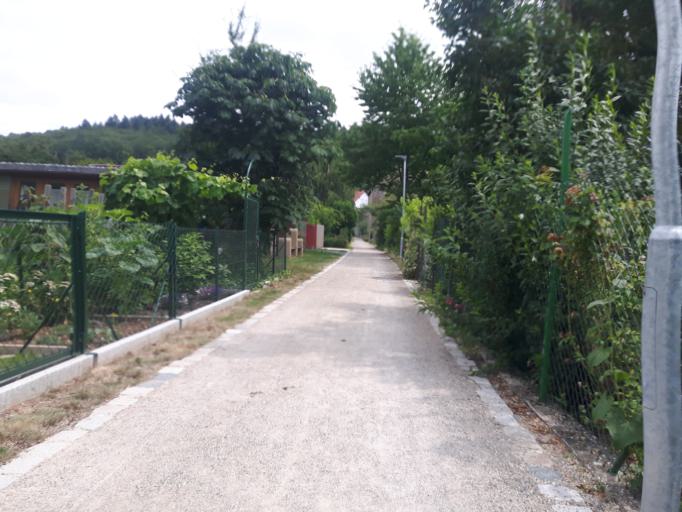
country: DE
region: Baden-Wuerttemberg
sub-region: Regierungsbezirk Stuttgart
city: Eppingen
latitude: 49.0979
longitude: 8.9034
